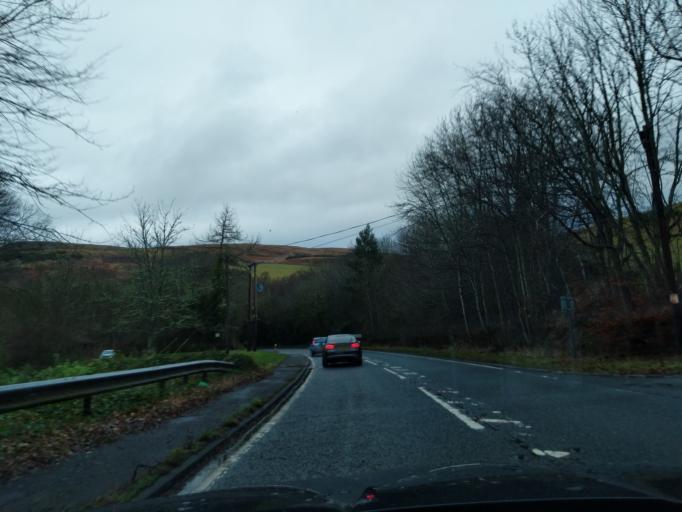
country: GB
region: Scotland
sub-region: The Scottish Borders
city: Galashiels
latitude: 55.6367
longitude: -2.8267
